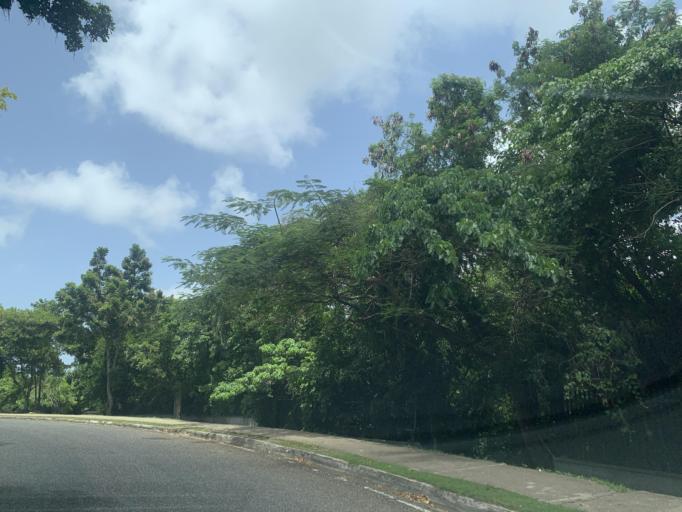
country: DO
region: Nacional
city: La Agustina
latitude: 18.4991
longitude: -69.9486
